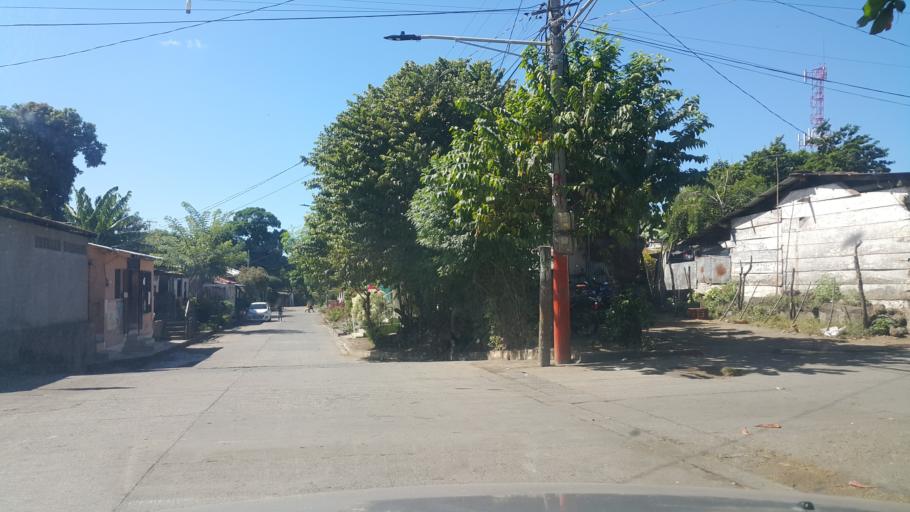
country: NI
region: Rivas
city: Moyogalpa
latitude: 11.5379
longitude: -85.6972
